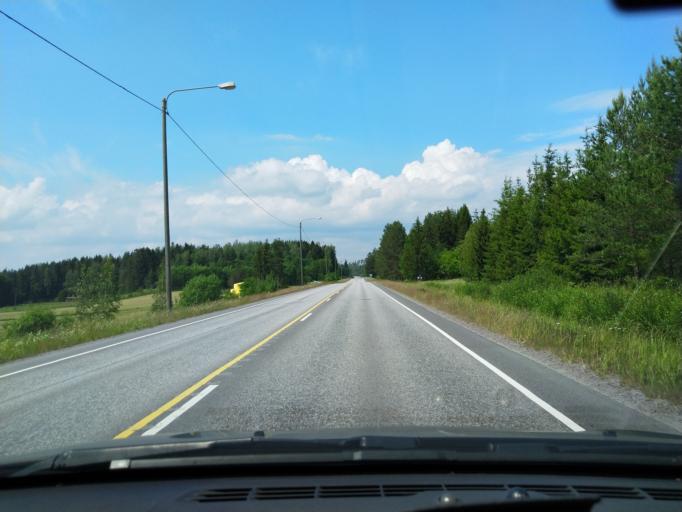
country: FI
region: Uusimaa
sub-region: Helsinki
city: Saukkola
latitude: 60.3785
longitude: 24.0969
